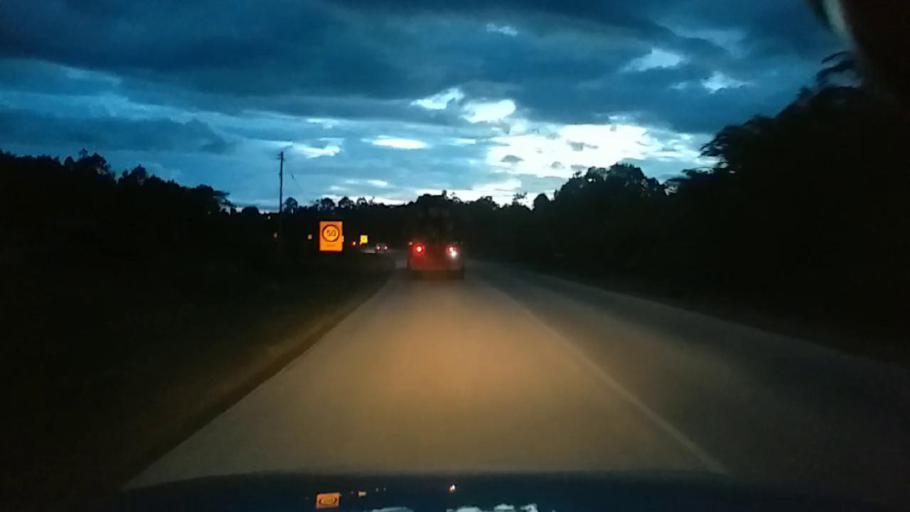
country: MY
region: Sarawak
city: Sibu
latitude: 2.4165
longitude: 112.1682
